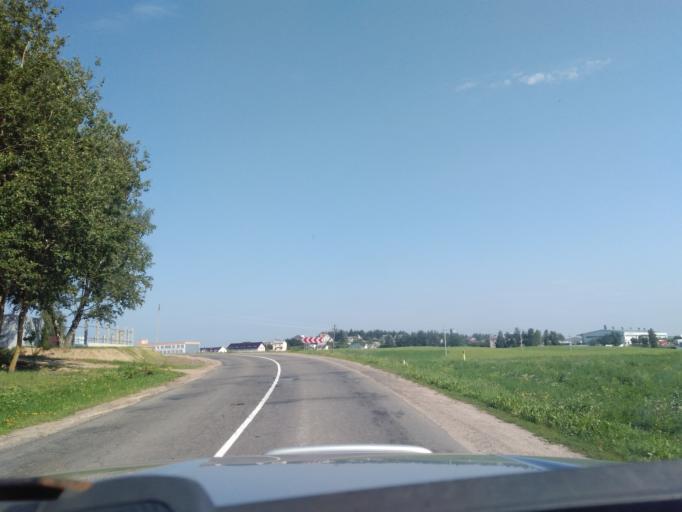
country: BY
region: Minsk
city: Zhdanovichy
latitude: 53.9304
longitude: 27.4184
